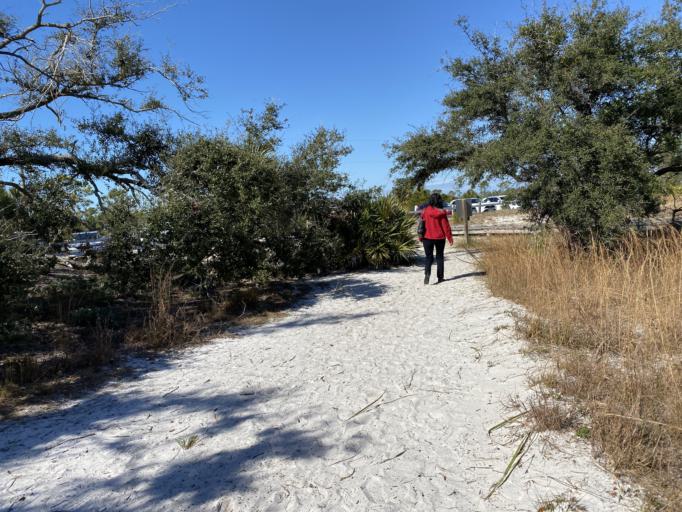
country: US
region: Florida
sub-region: Bay County
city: Lower Grand Lagoon
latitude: 30.1284
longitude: -85.7332
